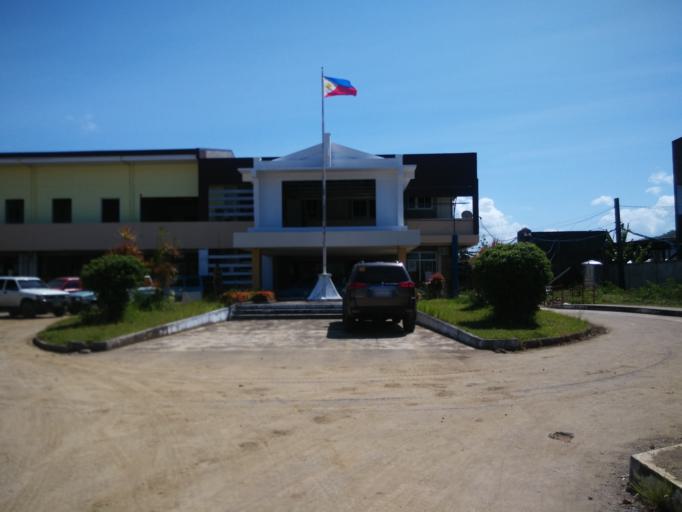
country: PH
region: Eastern Visayas
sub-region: Province of Leyte
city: Pawing
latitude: 11.1746
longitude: 125.0087
